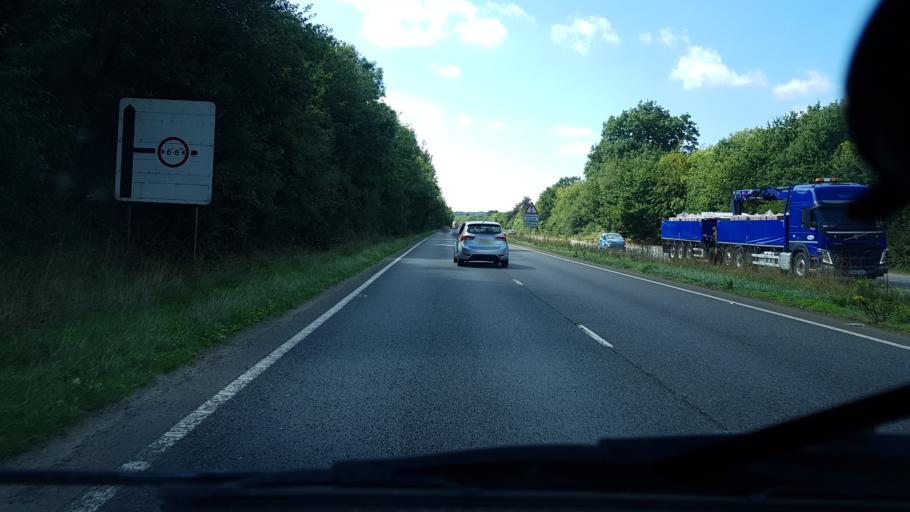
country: GB
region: England
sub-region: West Sussex
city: Horsham
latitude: 51.0880
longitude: -0.3076
